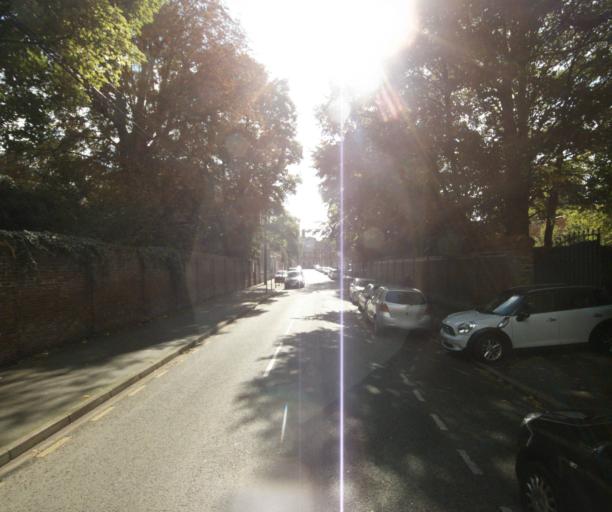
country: FR
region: Nord-Pas-de-Calais
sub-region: Departement du Nord
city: Loos
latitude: 50.6156
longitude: 3.0062
